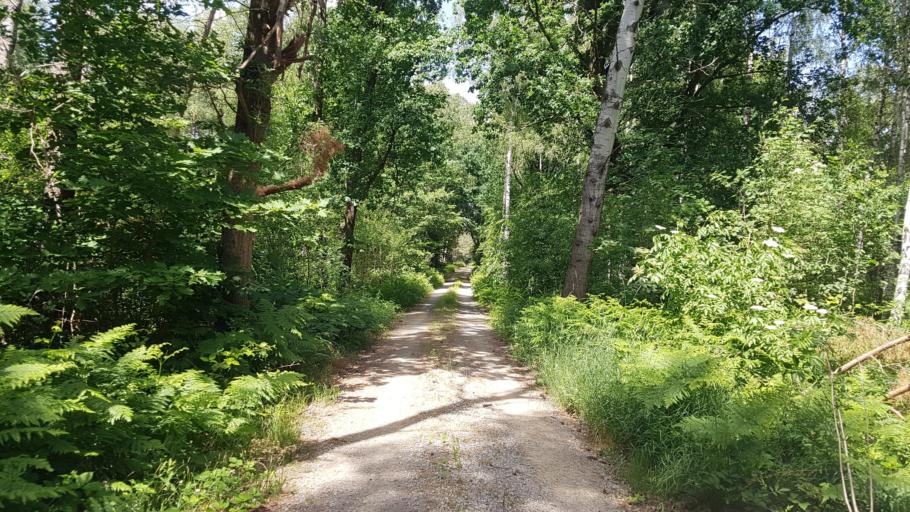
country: DE
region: Brandenburg
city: Plessa
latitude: 51.4907
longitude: 13.6116
